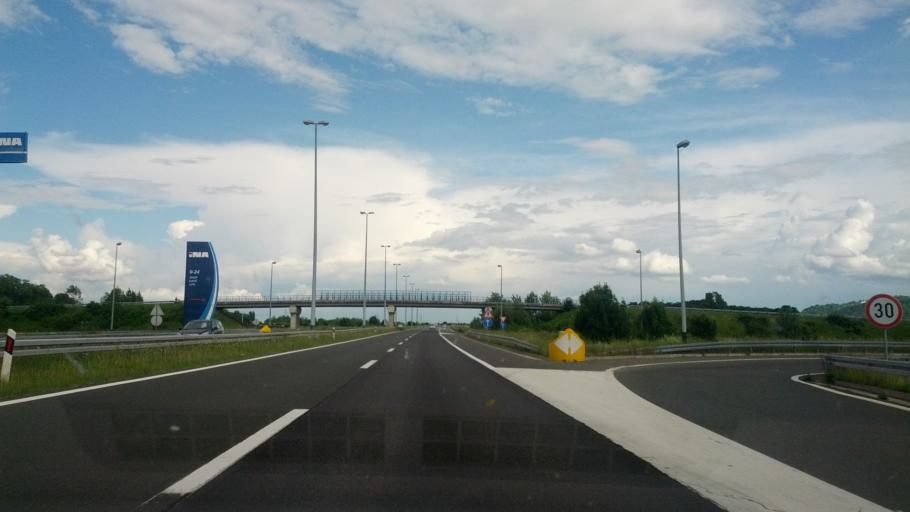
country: HR
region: Zagrebacka
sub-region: Grad Samobor
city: Samobor
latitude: 45.8261
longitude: 15.7384
